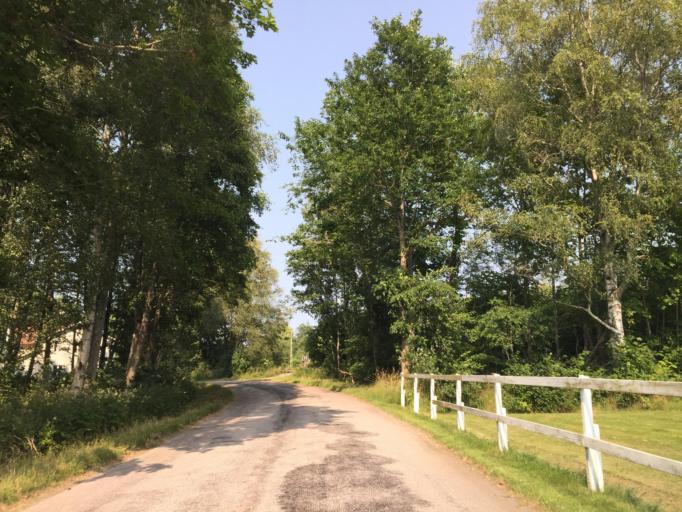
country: SE
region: Vaestra Goetaland
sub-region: Vanersborgs Kommun
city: Vanersborg
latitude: 58.3601
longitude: 12.2737
